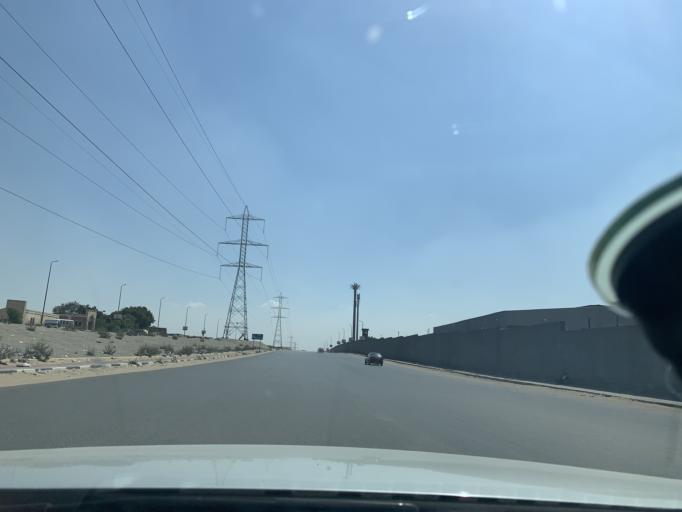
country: EG
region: Muhafazat al Qahirah
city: Cairo
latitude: 30.0352
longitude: 31.3540
